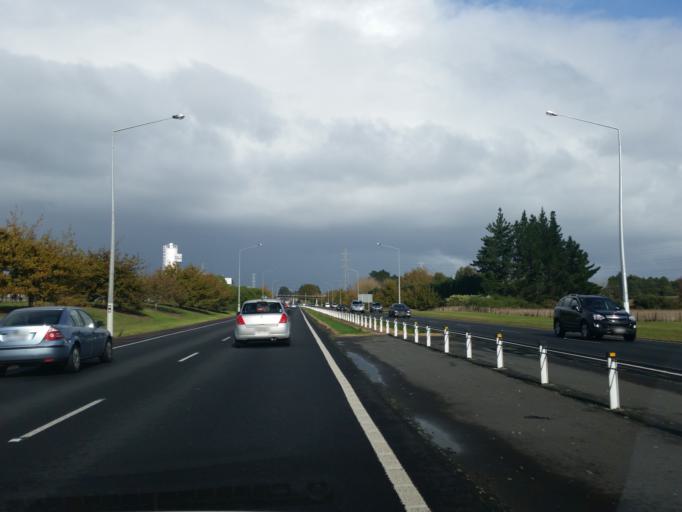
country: NZ
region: Auckland
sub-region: Auckland
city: Papakura
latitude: -37.0988
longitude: 174.9448
